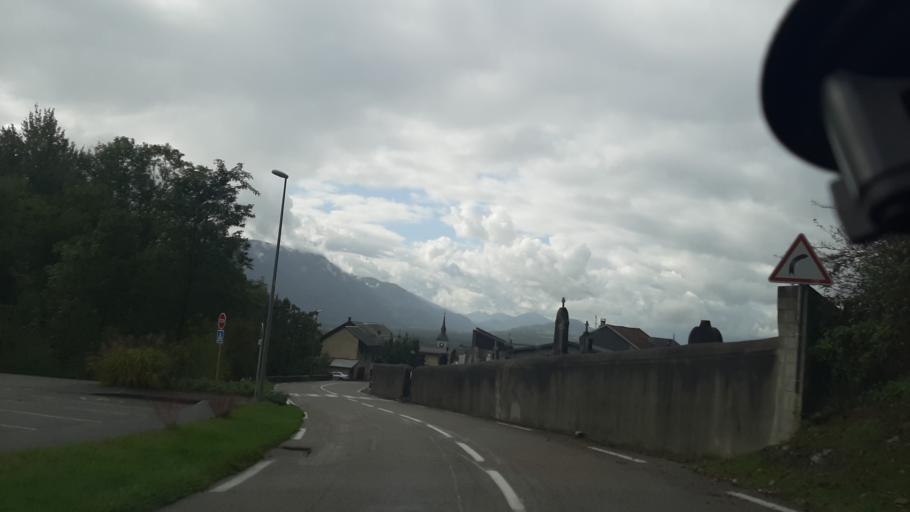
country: FR
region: Rhone-Alpes
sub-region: Departement de la Savoie
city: Gresy-sur-Isere
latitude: 45.6044
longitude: 6.2578
